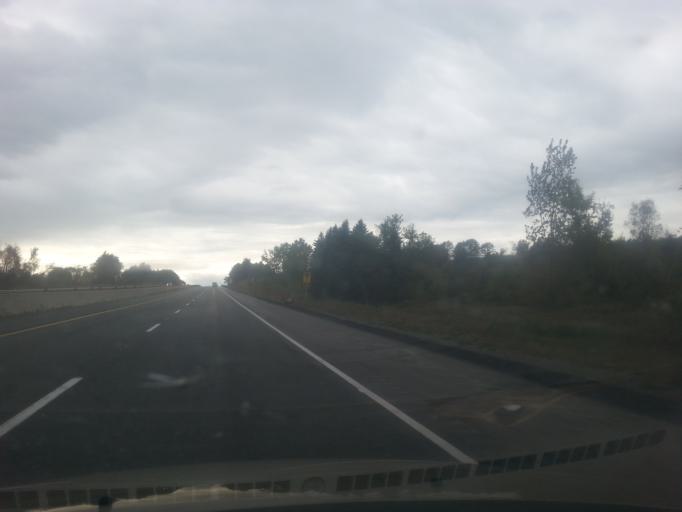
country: CA
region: Ontario
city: Quinte West
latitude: 44.0768
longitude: -77.7536
